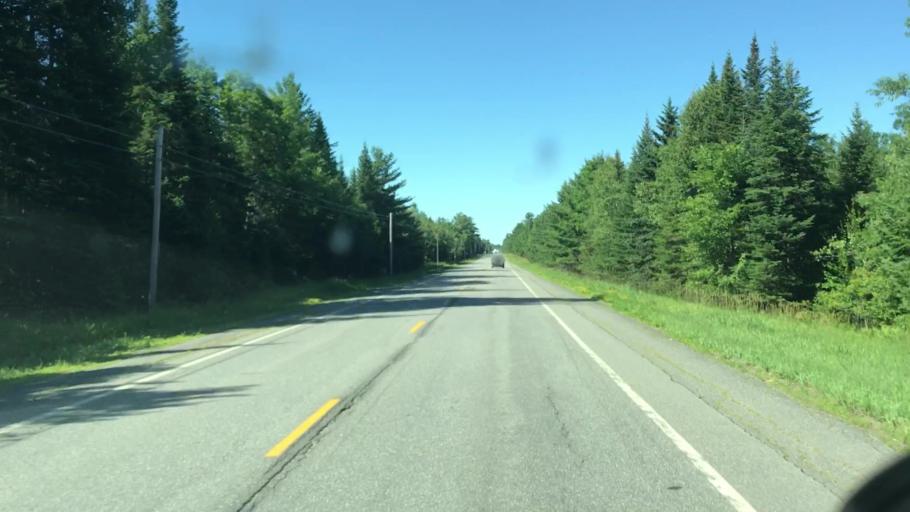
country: US
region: Maine
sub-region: Penobscot County
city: Enfield
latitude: 45.3104
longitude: -68.6082
